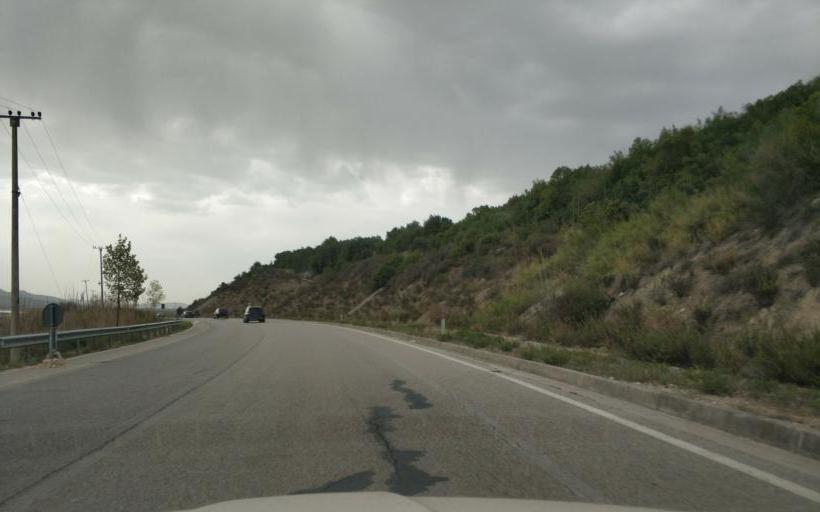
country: AL
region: Fier
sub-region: Rrethi i Mallakastres
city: Hekal
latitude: 40.5276
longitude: 19.7322
